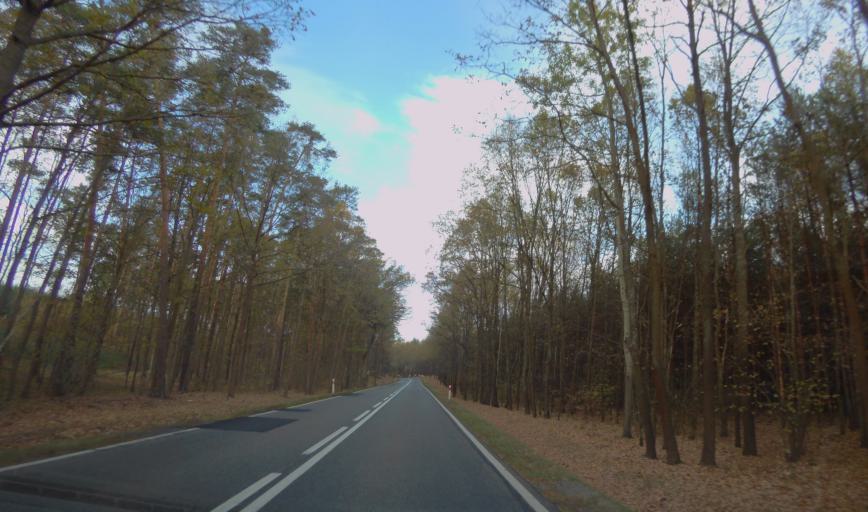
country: PL
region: Subcarpathian Voivodeship
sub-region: Powiat nizanski
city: Krzeszow
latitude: 50.3826
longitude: 22.3091
